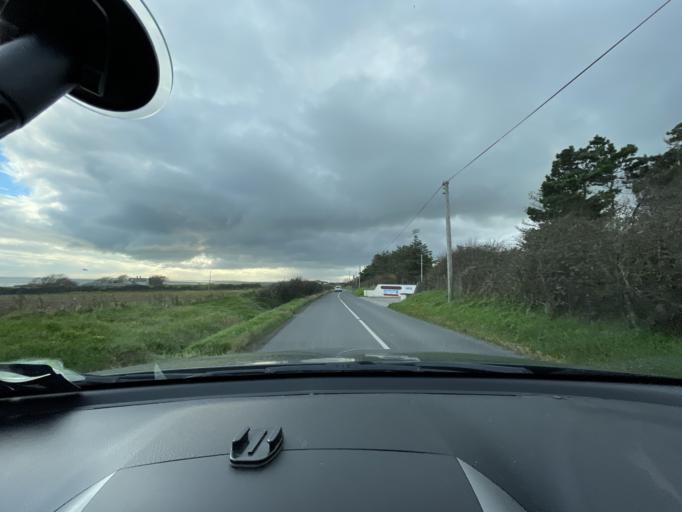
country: IE
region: Leinster
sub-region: Lu
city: Clogherhead
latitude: 53.7791
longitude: -6.2455
